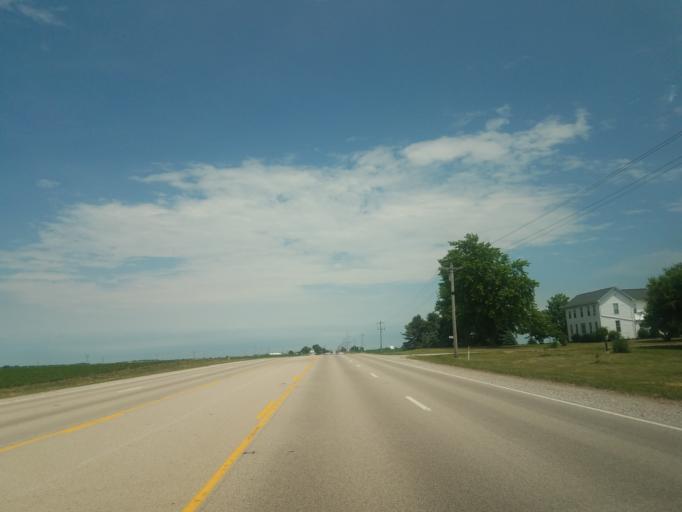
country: US
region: Illinois
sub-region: McLean County
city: Downs
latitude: 40.4281
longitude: -88.9013
